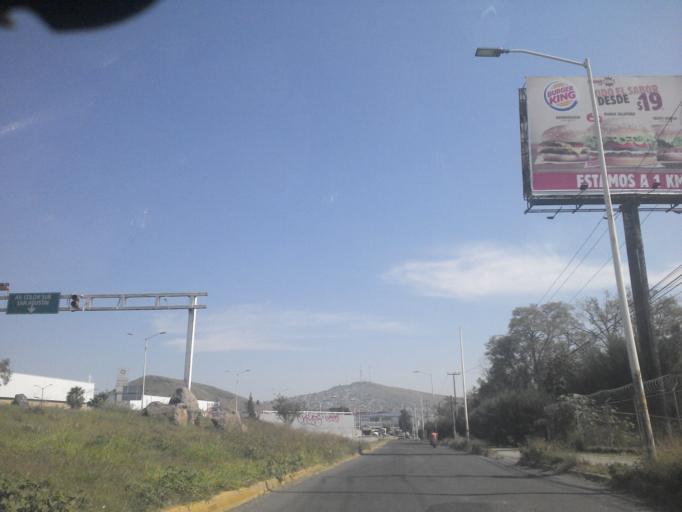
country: MX
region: Jalisco
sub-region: Tlajomulco de Zuniga
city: La Tijera
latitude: 20.6078
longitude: -103.4056
